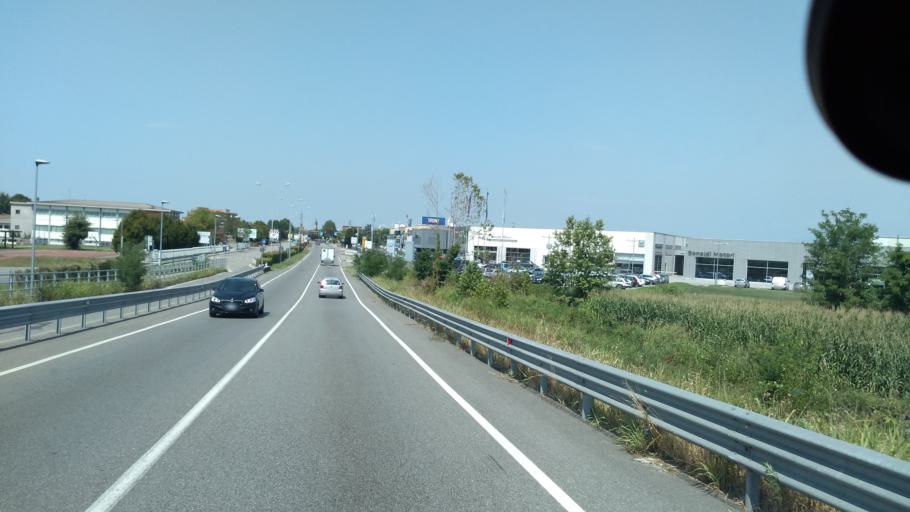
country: IT
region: Lombardy
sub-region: Provincia di Bergamo
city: Calvenzano
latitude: 45.5093
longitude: 9.6169
